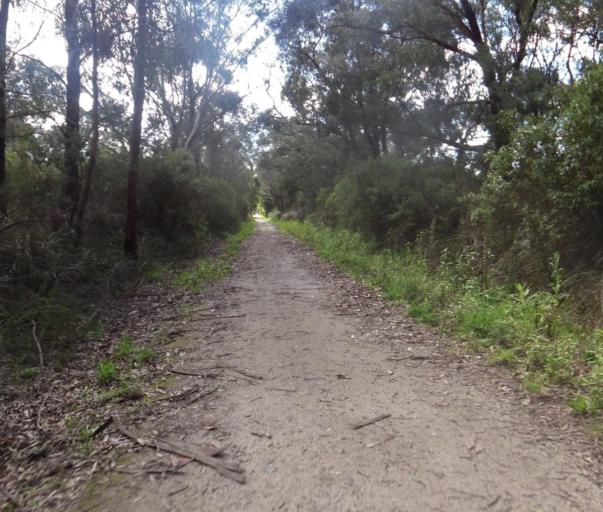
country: AU
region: Victoria
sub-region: Bass Coast
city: North Wonthaggi
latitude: -38.5815
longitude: 146.0334
